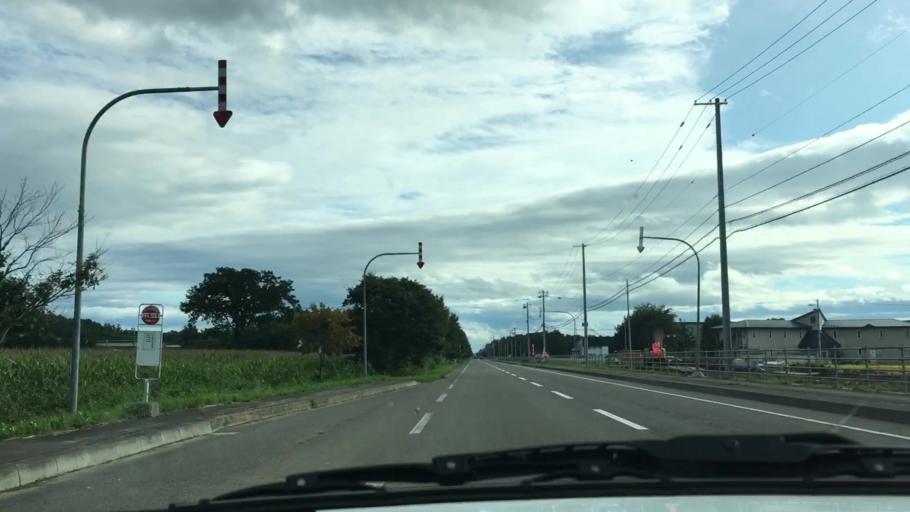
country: JP
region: Hokkaido
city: Otofuke
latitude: 43.2541
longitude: 143.2999
